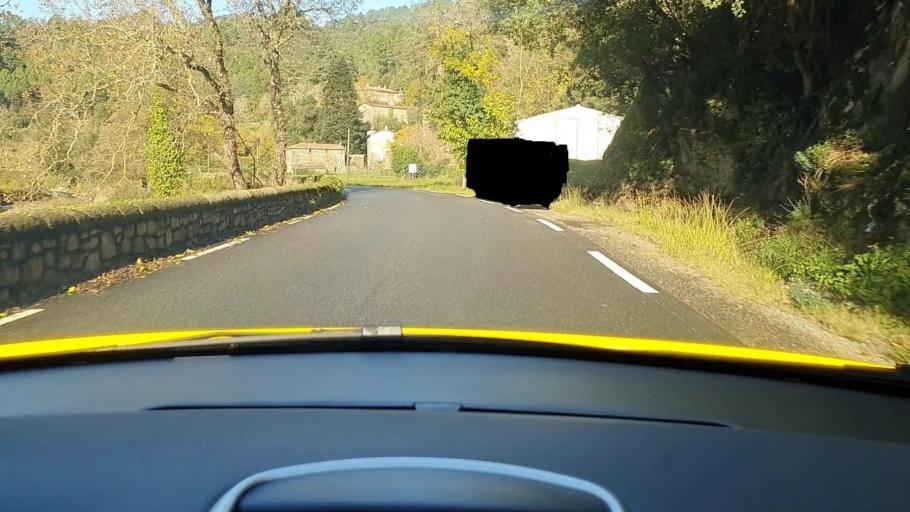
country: FR
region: Languedoc-Roussillon
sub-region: Departement du Gard
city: Valleraugue
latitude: 44.1365
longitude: 3.7522
